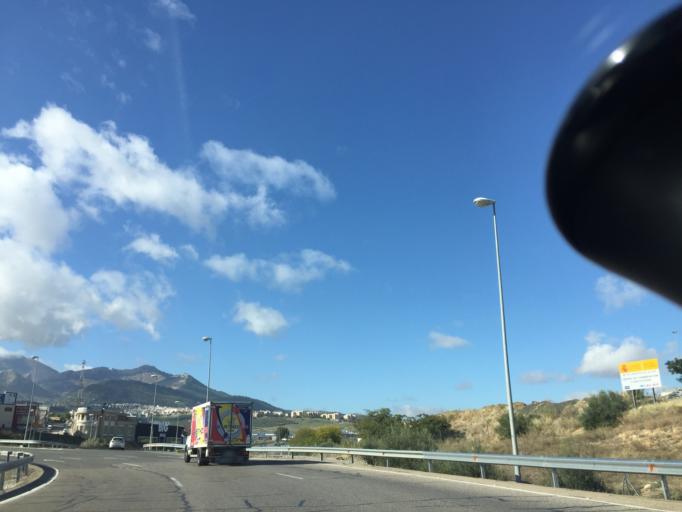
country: ES
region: Andalusia
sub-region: Provincia de Jaen
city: Jaen
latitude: 37.7825
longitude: -3.7565
